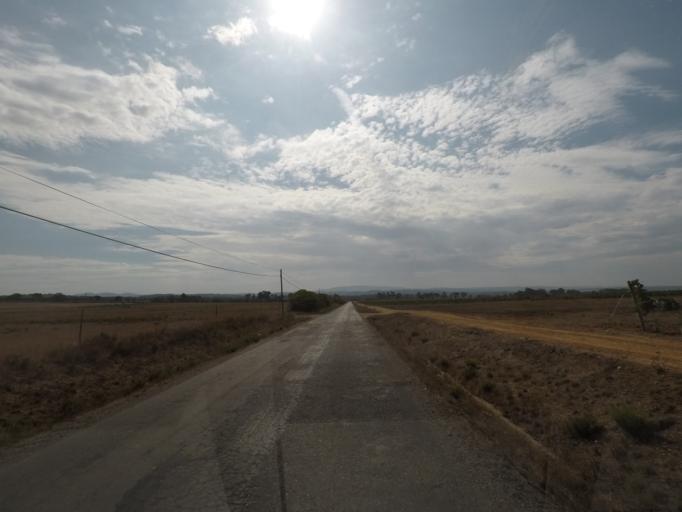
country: PT
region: Beja
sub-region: Odemira
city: Sao Teotonio
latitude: 37.4717
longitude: -8.7557
